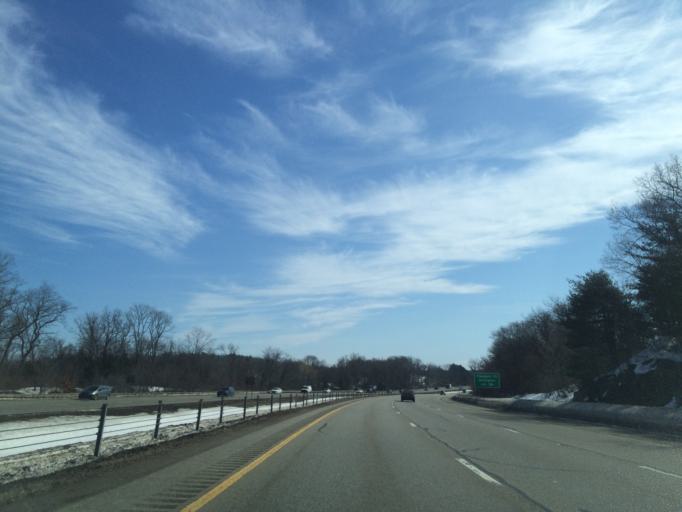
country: US
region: Massachusetts
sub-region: Middlesex County
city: Lexington
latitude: 42.4214
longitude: -71.2258
